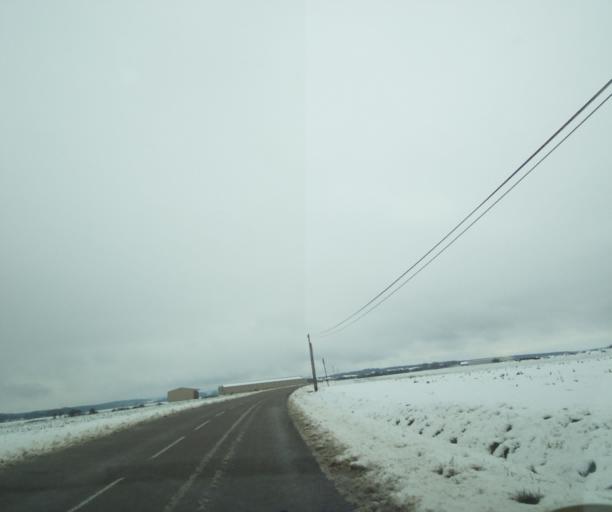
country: FR
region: Champagne-Ardenne
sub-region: Departement de la Haute-Marne
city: Montier-en-Der
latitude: 48.4468
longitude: 4.8003
